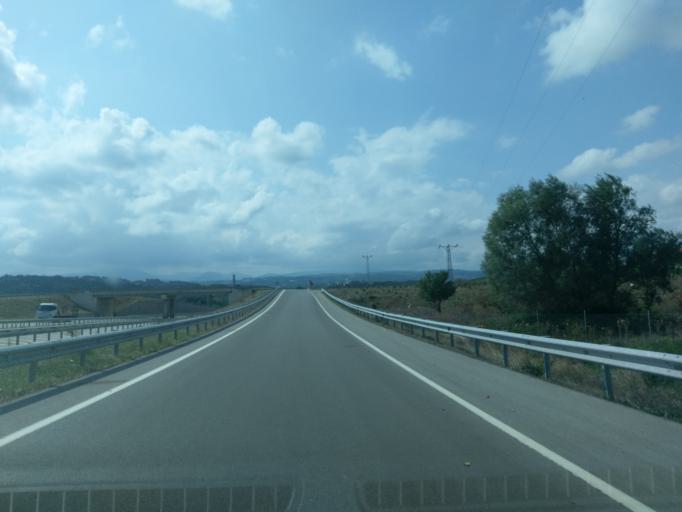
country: TR
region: Sinop
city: Kabali
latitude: 41.9293
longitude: 35.0844
